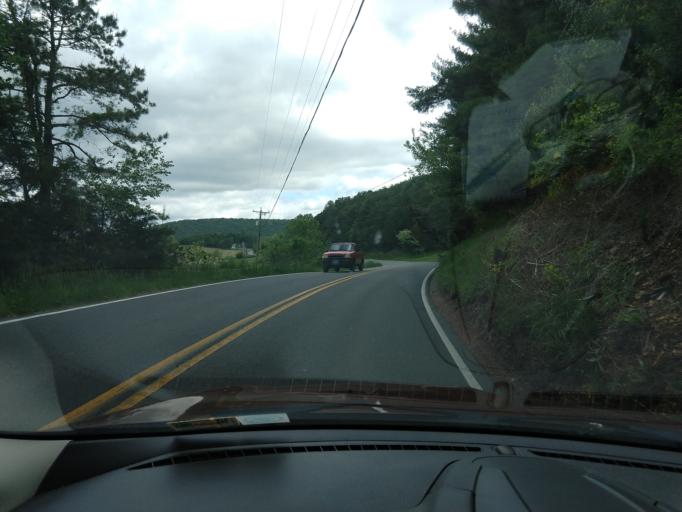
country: US
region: Virginia
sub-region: Wythe County
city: Wytheville
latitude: 36.9031
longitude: -80.9691
